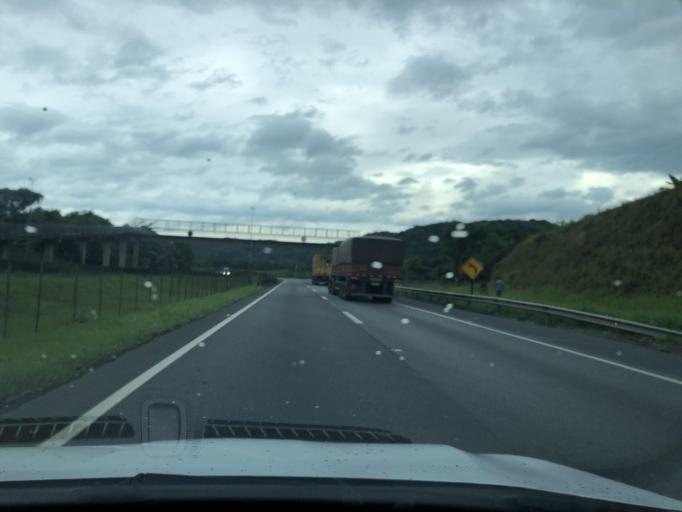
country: BR
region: Sao Paulo
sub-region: Miracatu
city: Miracatu
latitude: -24.2464
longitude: -47.4382
